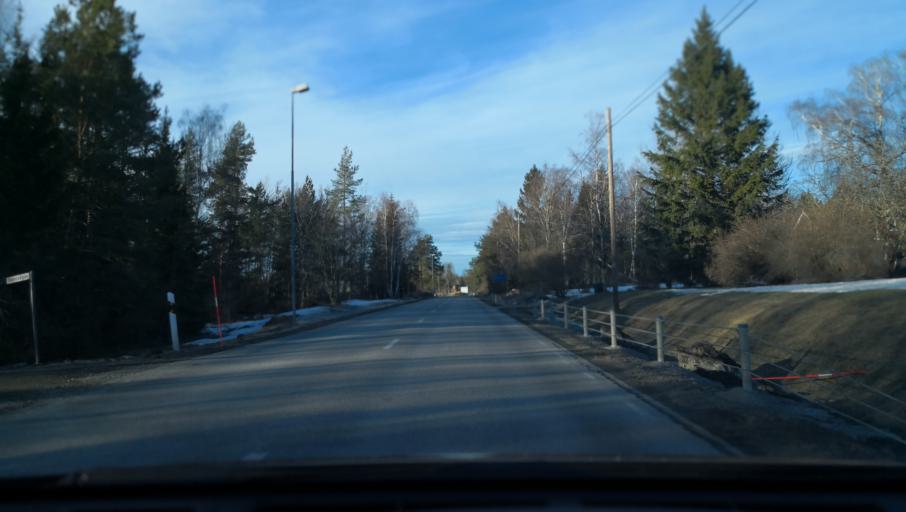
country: SE
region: Uppsala
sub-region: Osthammars Kommun
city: OEsthammar
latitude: 60.2930
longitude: 18.2846
